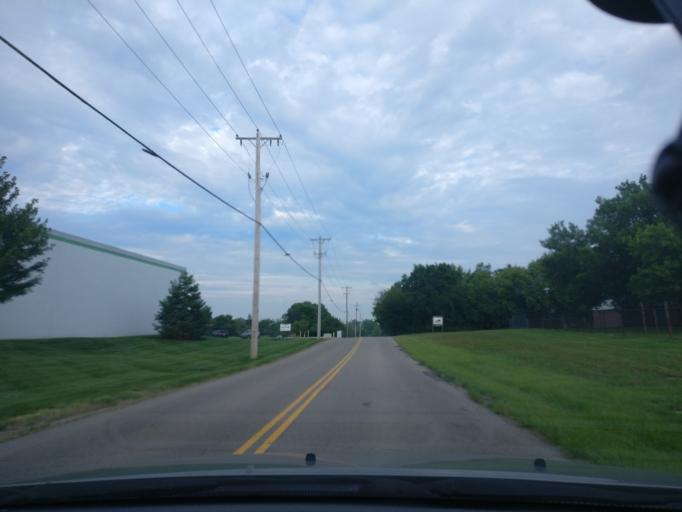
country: US
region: Ohio
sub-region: Montgomery County
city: West Carrollton City
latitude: 39.6298
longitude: -84.2376
